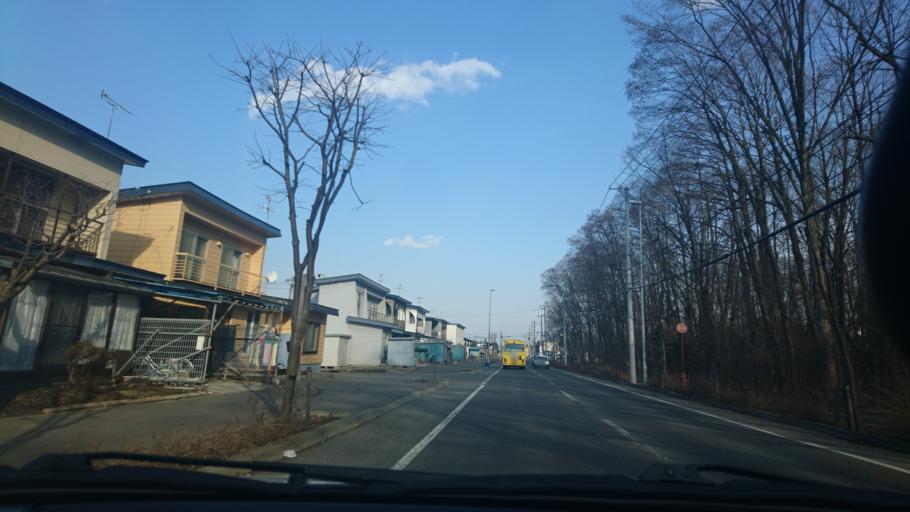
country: JP
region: Hokkaido
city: Obihiro
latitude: 42.9244
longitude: 143.1736
